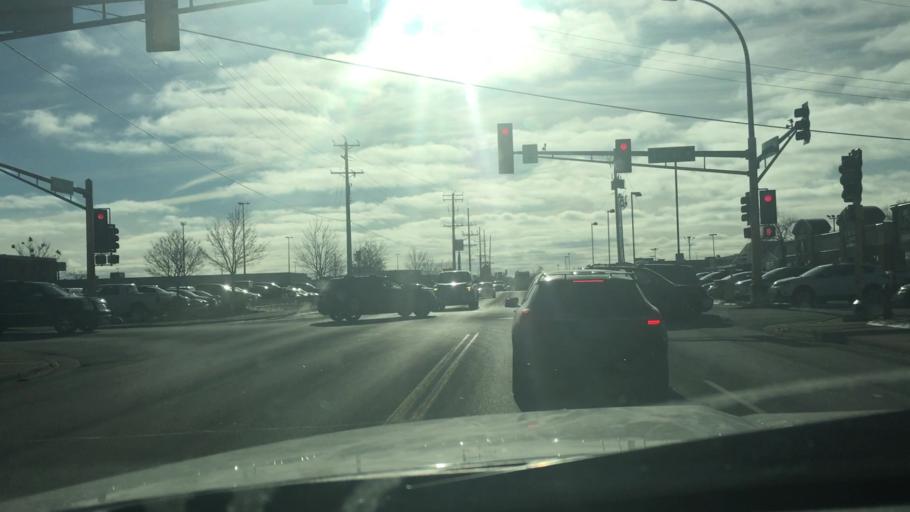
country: US
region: Minnesota
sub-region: Stearns County
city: Waite Park
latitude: 45.5564
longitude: -94.2138
